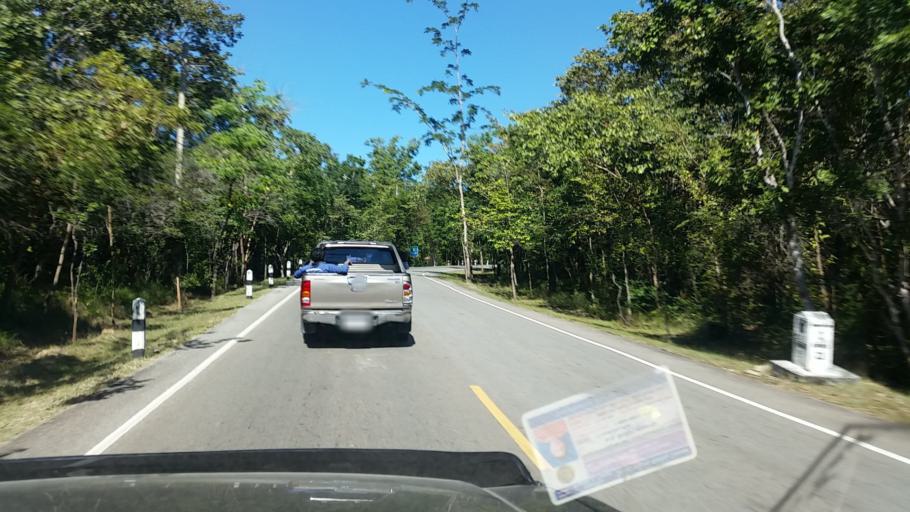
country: TH
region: Chaiyaphum
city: Chaiyaphum
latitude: 15.9699
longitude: 102.0244
